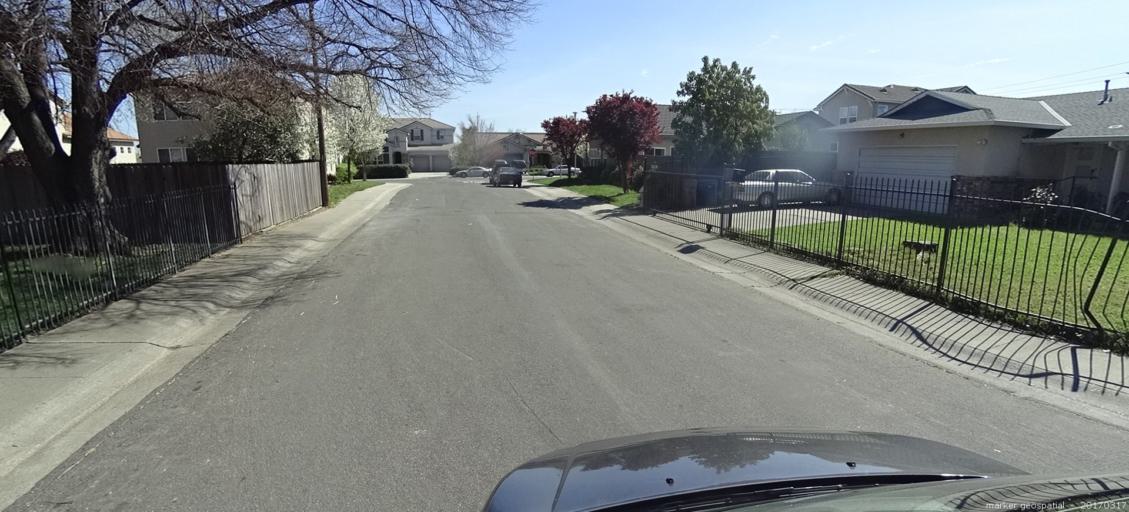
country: US
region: California
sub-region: Sacramento County
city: Parkway
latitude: 38.4822
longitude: -121.4859
